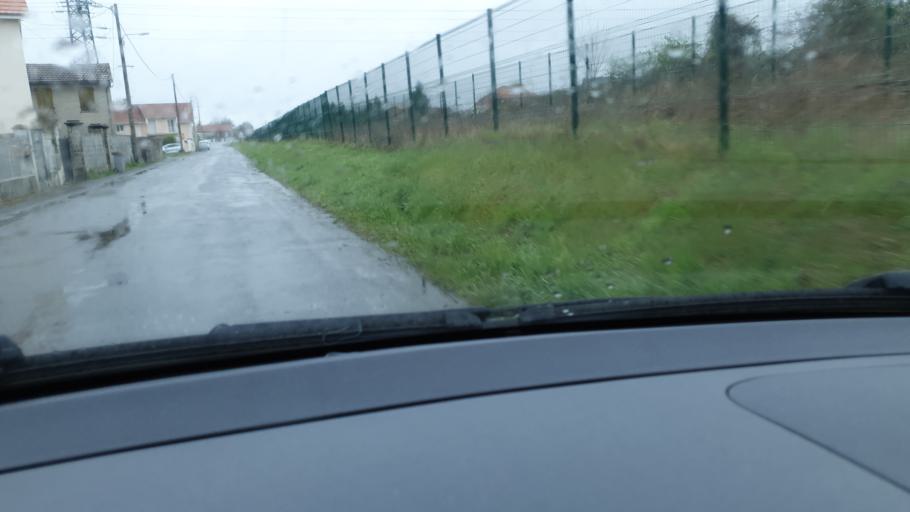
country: FR
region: Midi-Pyrenees
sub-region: Departement des Hautes-Pyrenees
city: Tarbes
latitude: 43.2503
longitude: 0.0536
